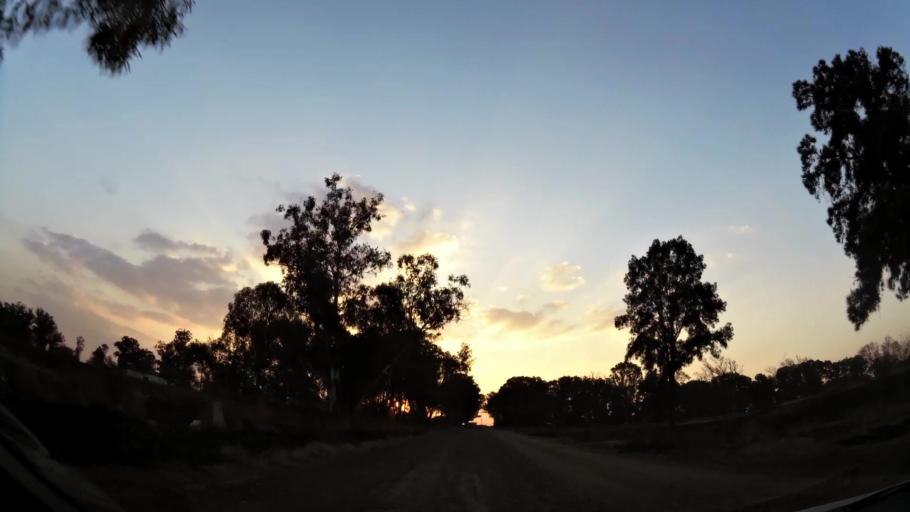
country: ZA
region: Gauteng
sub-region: Ekurhuleni Metropolitan Municipality
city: Springs
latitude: -26.3312
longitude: 28.4325
